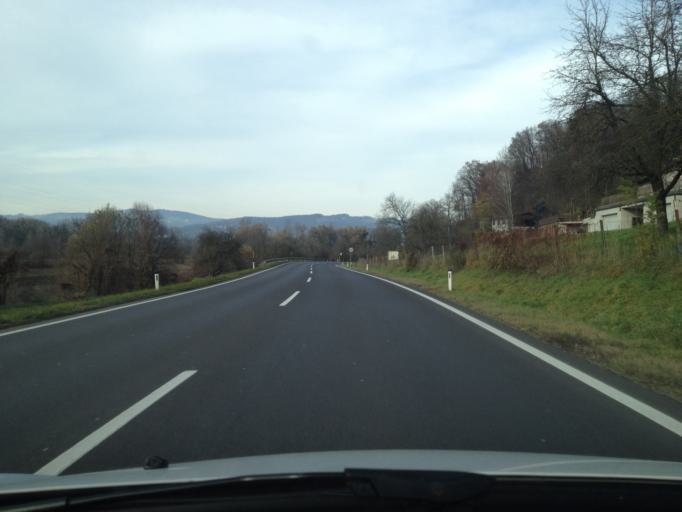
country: AT
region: Upper Austria
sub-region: Politischer Bezirk Urfahr-Umgebung
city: Steyregg
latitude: 48.3109
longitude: 14.3360
